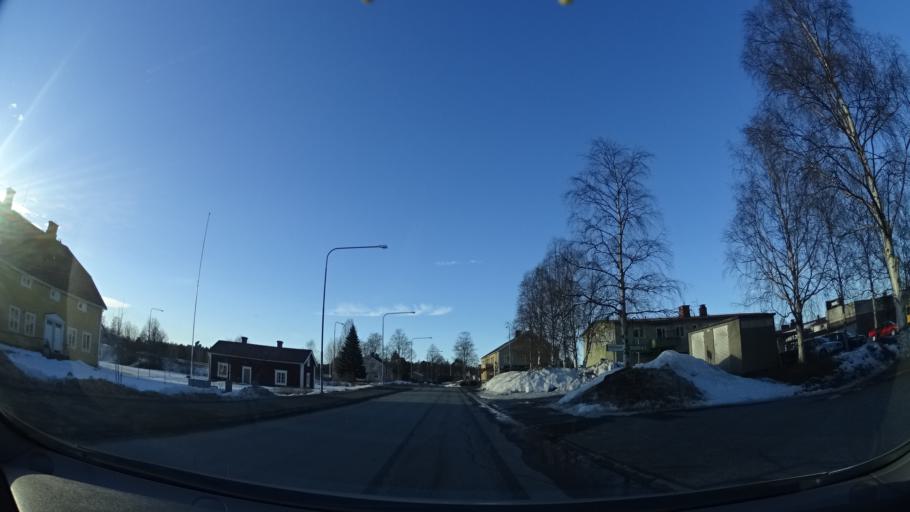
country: SE
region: Vaesterbotten
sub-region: Skelleftea Kommun
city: Byske
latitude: 64.9514
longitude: 21.2033
